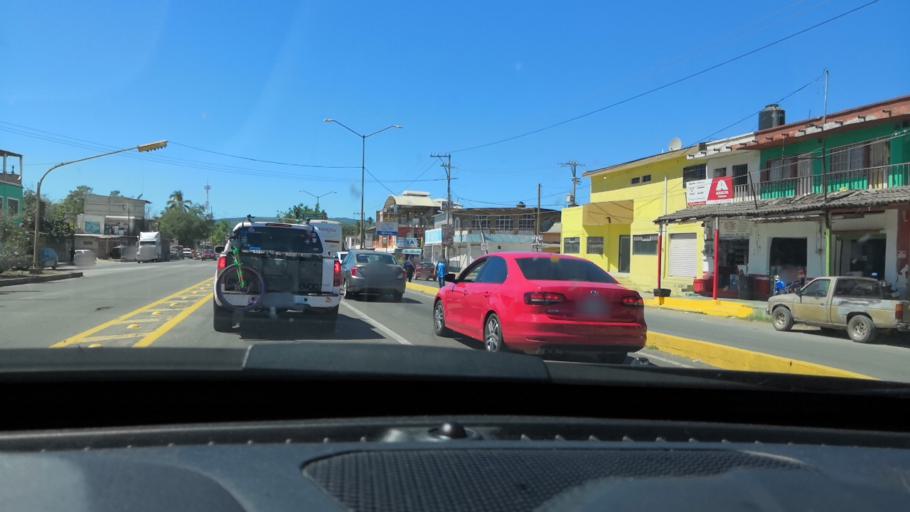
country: MX
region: Nayarit
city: Las Varas
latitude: 21.1785
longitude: -105.1383
